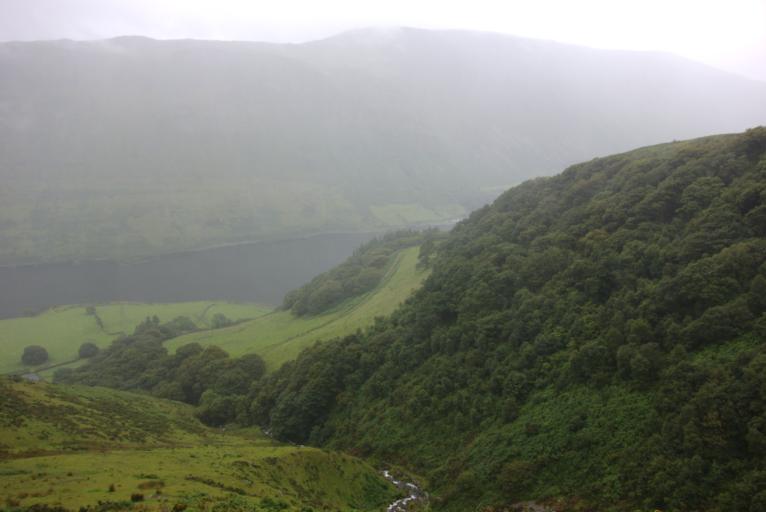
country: GB
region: Wales
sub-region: Gwynedd
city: Dolgellau
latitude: 52.6788
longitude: -3.9056
